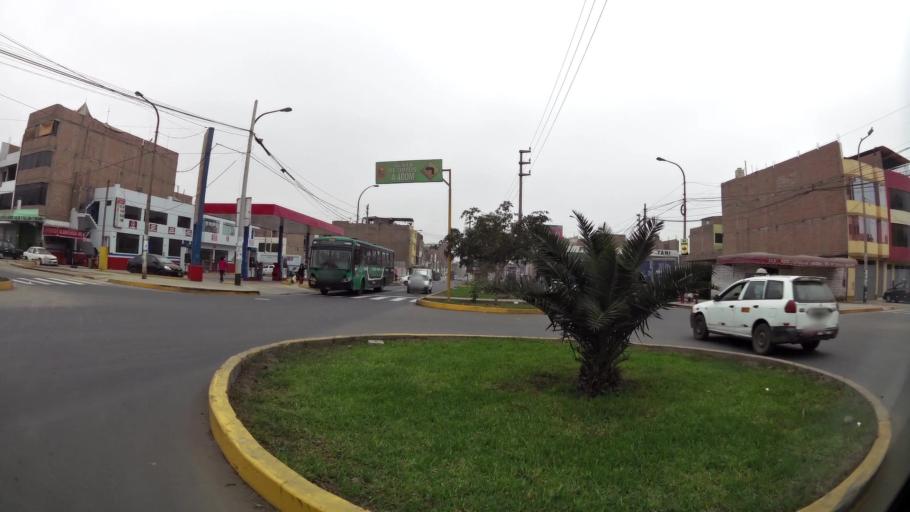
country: PE
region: Lima
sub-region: Lima
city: Urb. Santo Domingo
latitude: -11.8823
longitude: -77.0332
